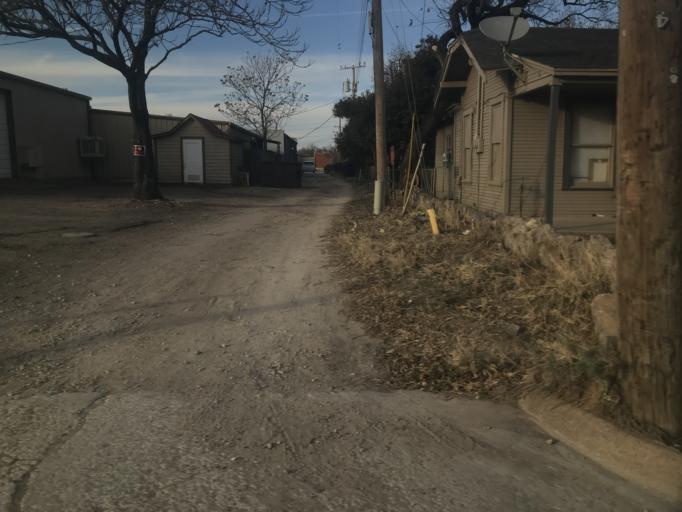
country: US
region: Texas
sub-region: Taylor County
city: Abilene
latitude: 32.4322
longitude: -99.7380
